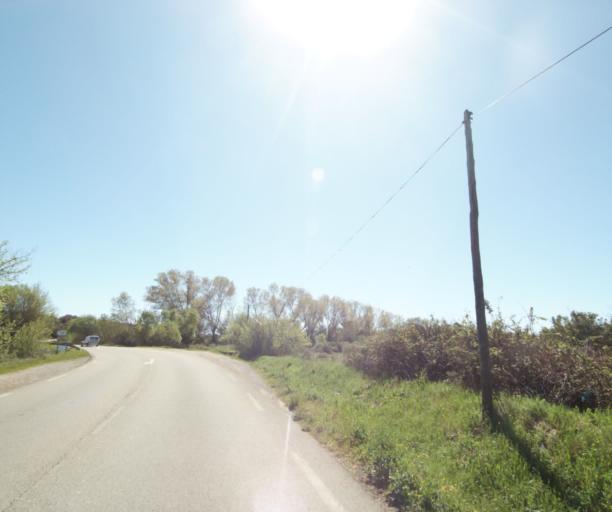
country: FR
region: Languedoc-Roussillon
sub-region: Departement de l'Herault
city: Saint-Jean-de-Vedas
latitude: 43.5597
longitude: 3.8502
